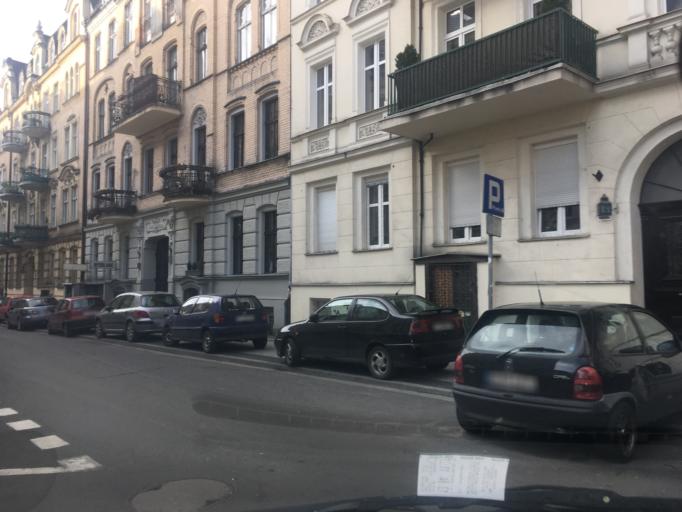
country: PL
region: Greater Poland Voivodeship
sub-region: Poznan
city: Poznan
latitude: 52.4028
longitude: 16.9330
